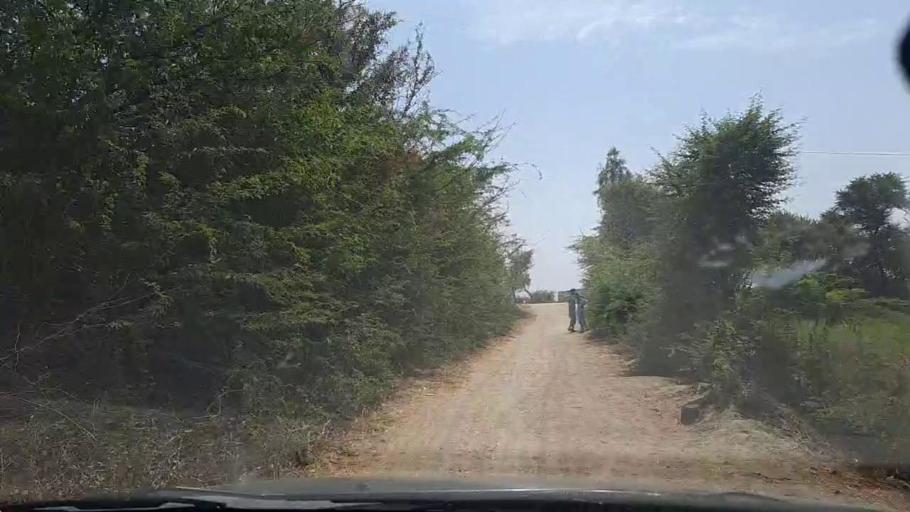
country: PK
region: Sindh
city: Mirpur Batoro
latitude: 24.6402
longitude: 68.1627
